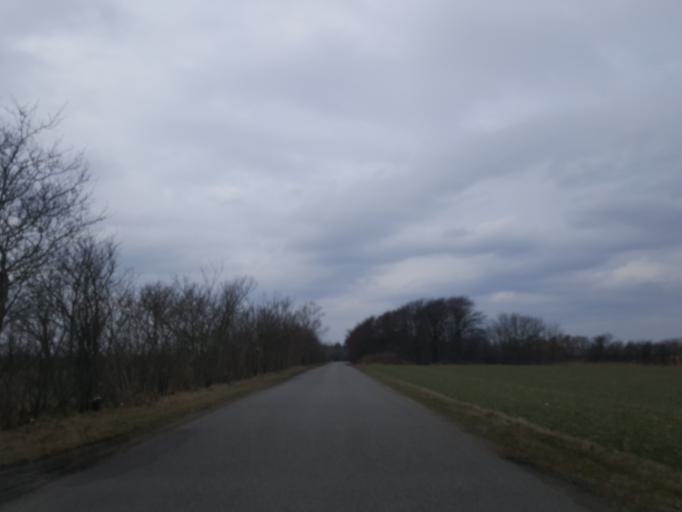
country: DK
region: Central Jutland
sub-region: Holstebro Kommune
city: Ulfborg
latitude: 56.3661
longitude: 8.2405
